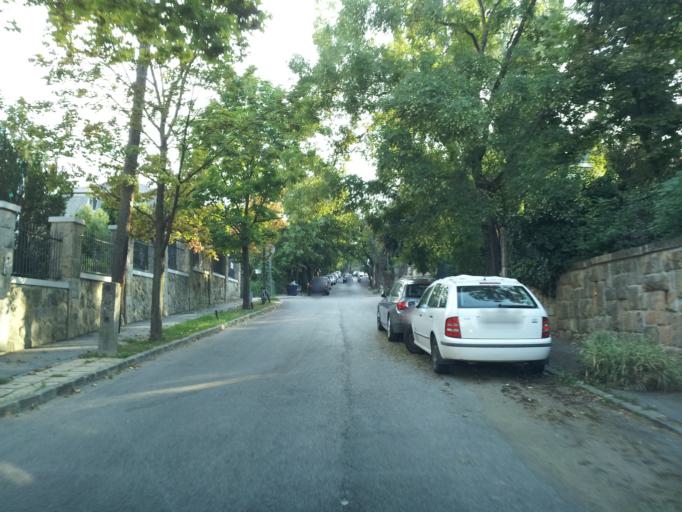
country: HU
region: Budapest
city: Budapest XII. keruelet
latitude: 47.5003
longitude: 19.0175
